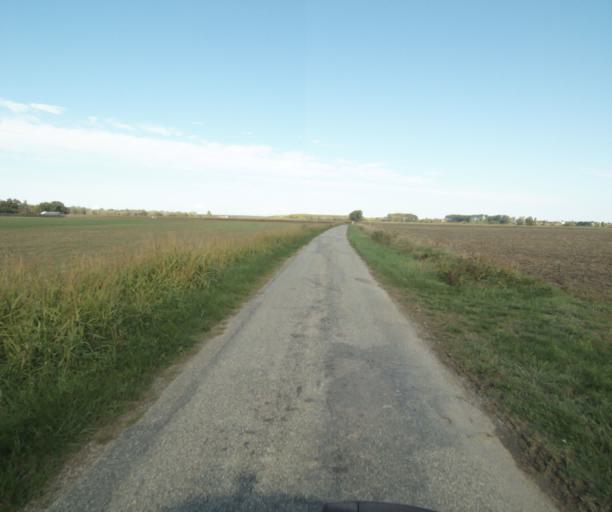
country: FR
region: Midi-Pyrenees
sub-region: Departement du Tarn-et-Garonne
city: Finhan
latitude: 43.8872
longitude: 1.2209
